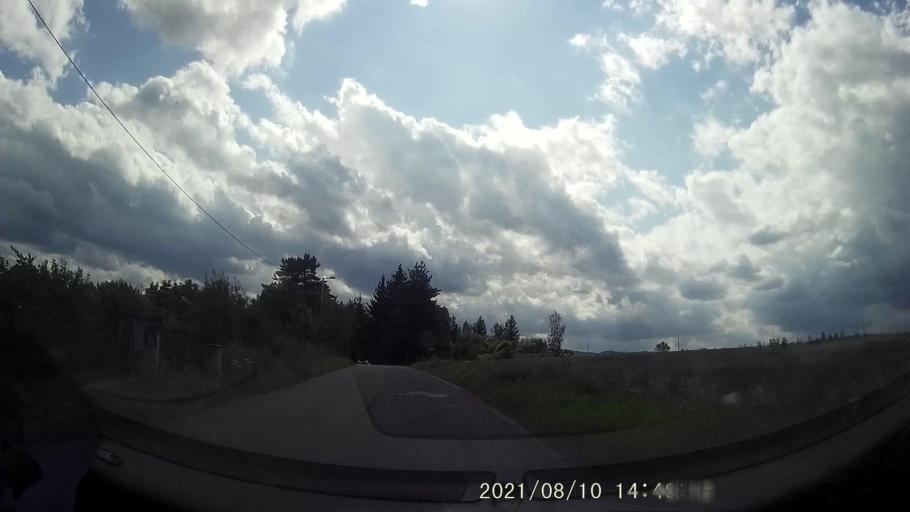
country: PL
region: Lower Silesian Voivodeship
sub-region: Powiat klodzki
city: Radkow
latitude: 50.5303
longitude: 16.4133
